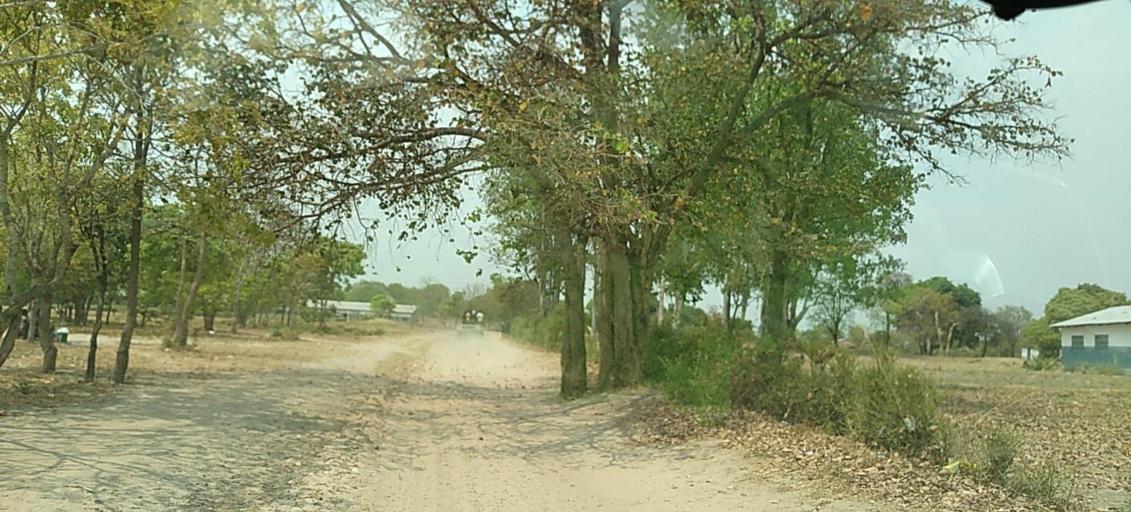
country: ZM
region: North-Western
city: Kabompo
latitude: -13.4957
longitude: 24.4659
